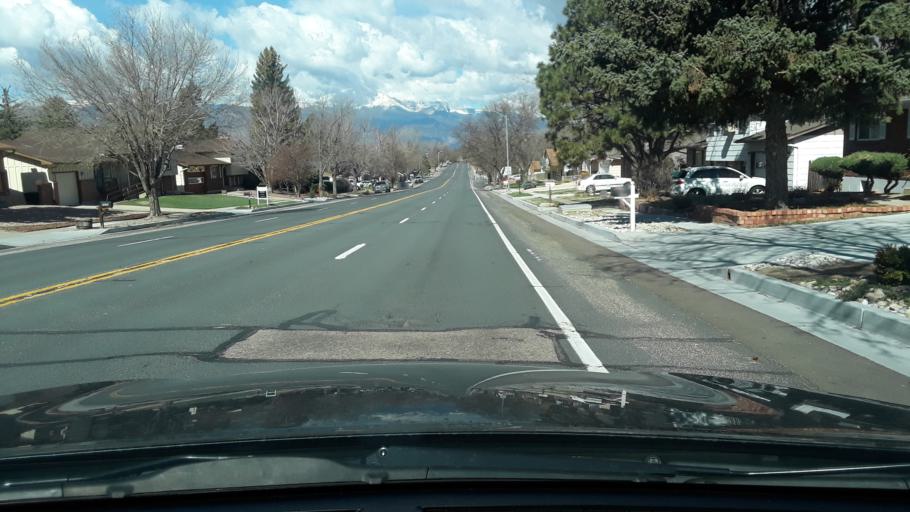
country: US
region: Colorado
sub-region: El Paso County
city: Cimarron Hills
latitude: 38.8542
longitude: -104.7330
